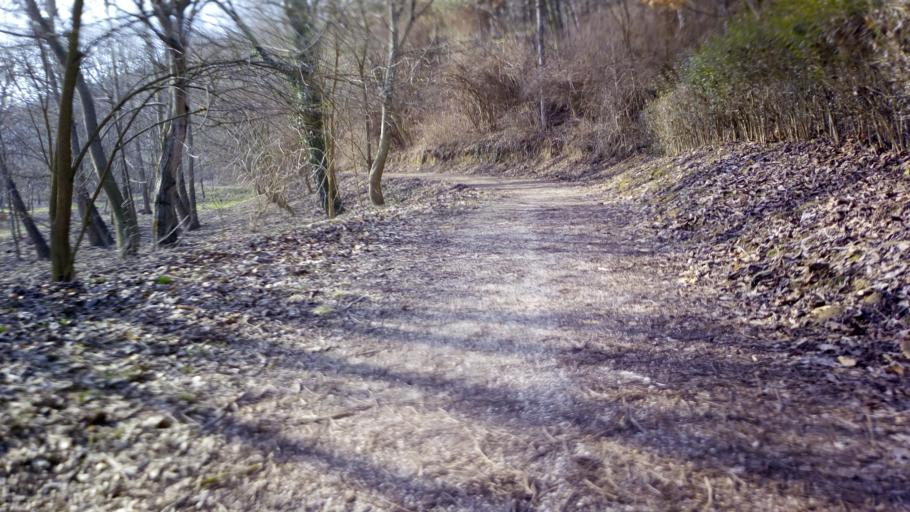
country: HU
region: Baranya
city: Pellerd
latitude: 46.0137
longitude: 18.1986
